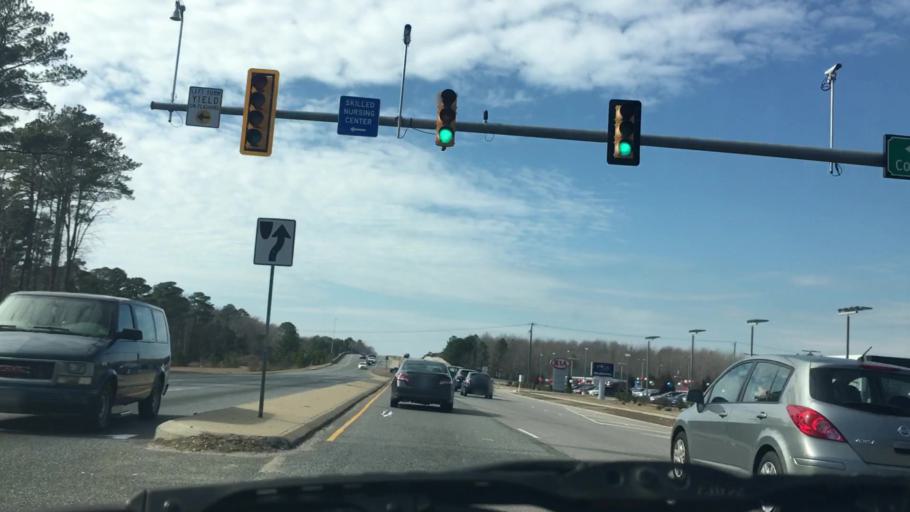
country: US
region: Virginia
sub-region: City of Portsmouth
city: Portsmouth Heights
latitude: 36.8655
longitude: -76.4226
